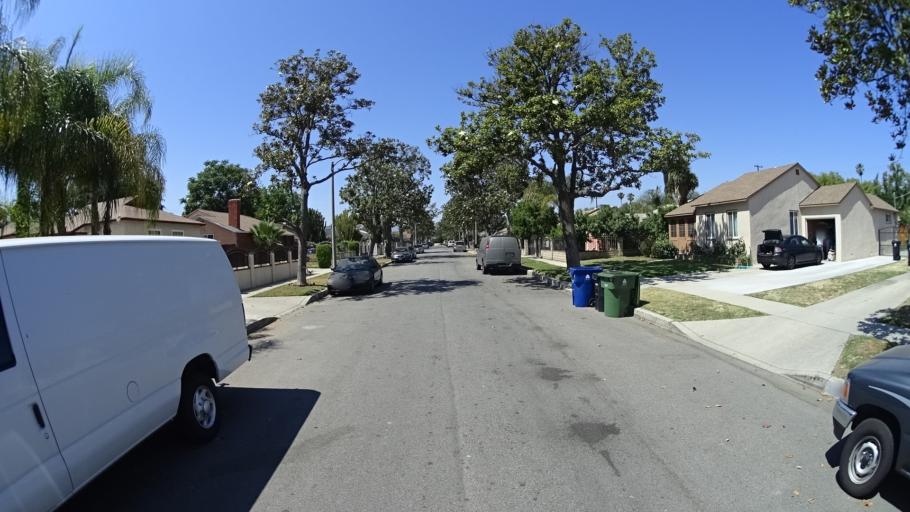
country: US
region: California
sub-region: Los Angeles County
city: Van Nuys
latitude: 34.2144
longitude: -118.4400
